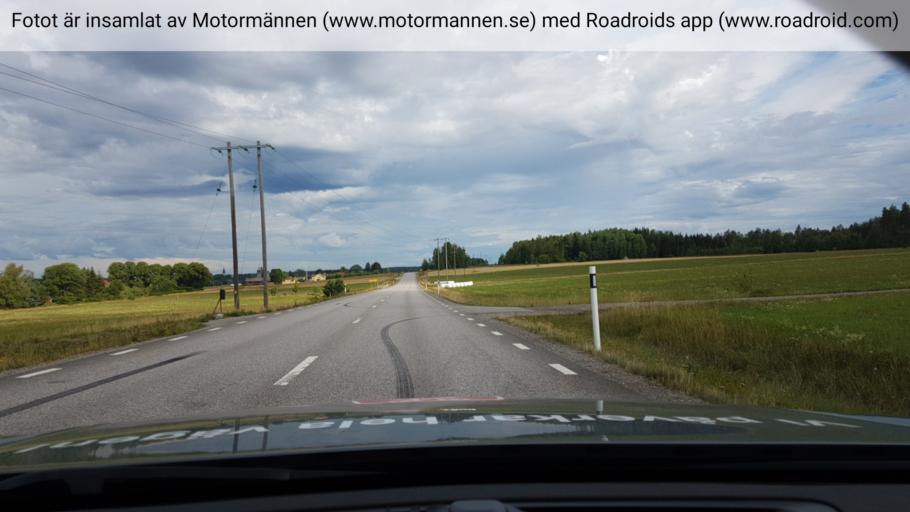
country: SE
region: Uppsala
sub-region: Heby Kommun
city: Heby
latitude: 59.9190
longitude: 16.8836
